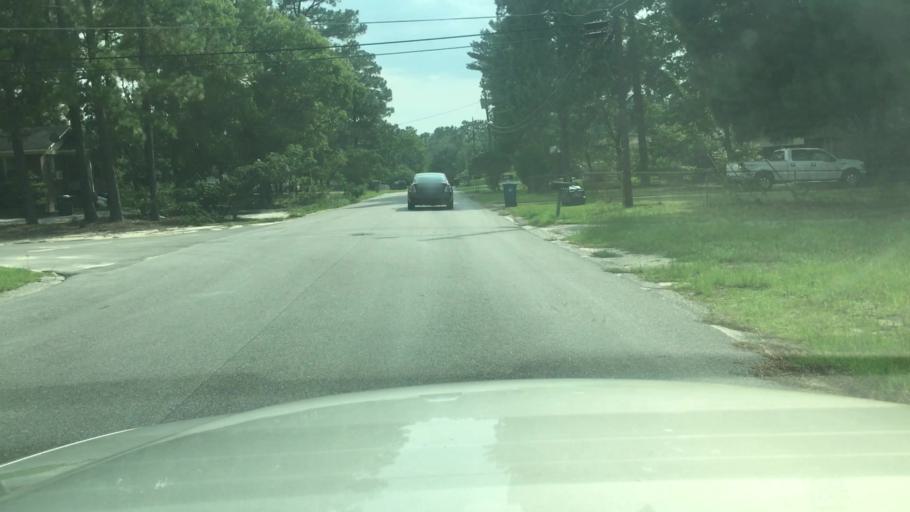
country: US
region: North Carolina
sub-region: Cumberland County
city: Fort Bragg
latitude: 35.0978
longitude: -79.0180
